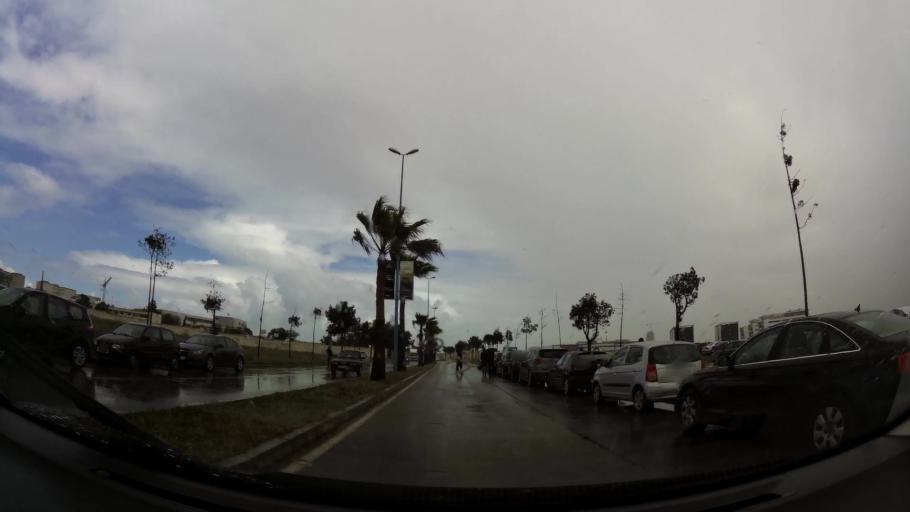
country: MA
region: Grand Casablanca
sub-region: Casablanca
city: Casablanca
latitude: 33.5480
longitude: -7.6700
